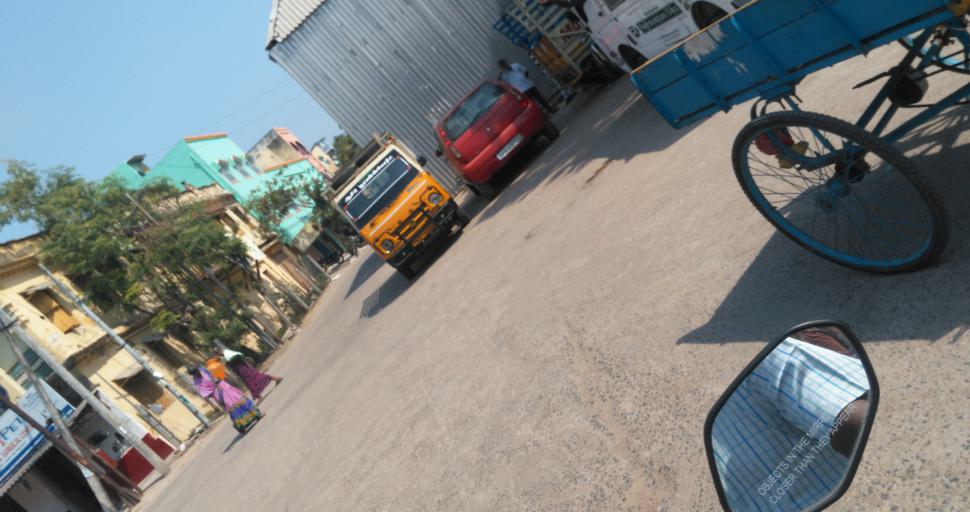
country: IN
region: Tamil Nadu
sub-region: Kancheepuram
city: Kanchipuram
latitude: 12.8443
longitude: 79.7014
